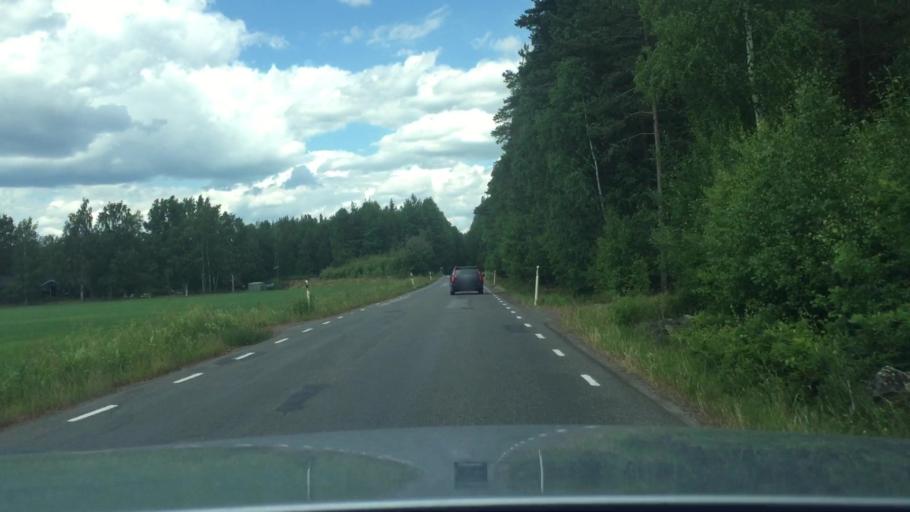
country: SE
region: Vaestra Goetaland
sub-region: Tidaholms Kommun
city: Tidaholm
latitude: 58.1990
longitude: 13.9791
